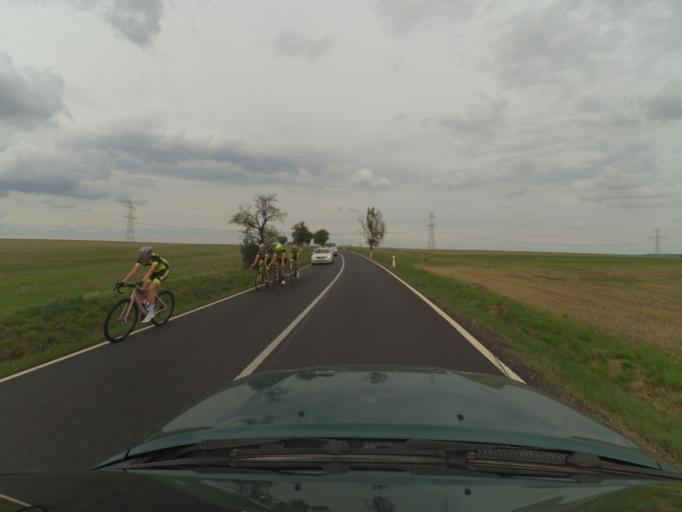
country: CZ
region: Ustecky
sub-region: Okres Louny
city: Louny
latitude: 50.3014
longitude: 13.7894
